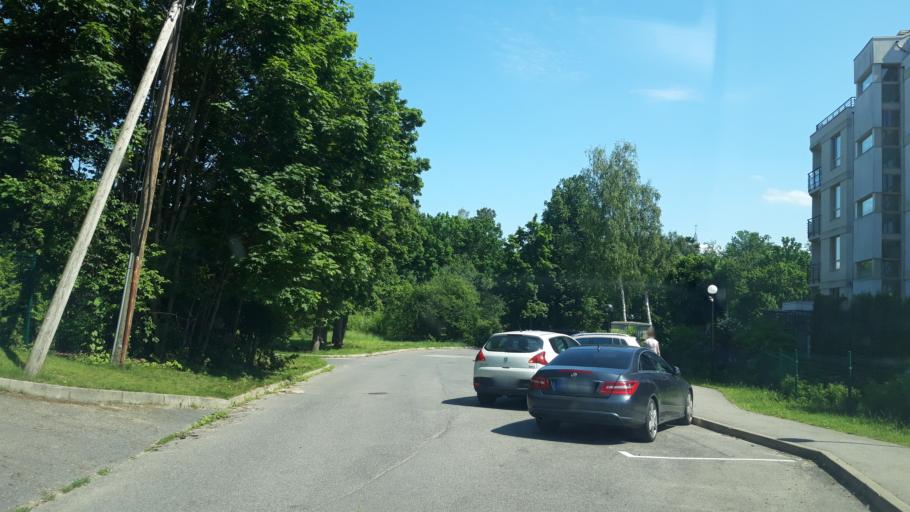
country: LV
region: Saulkrastu
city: Saulkrasti
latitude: 57.2597
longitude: 24.4134
